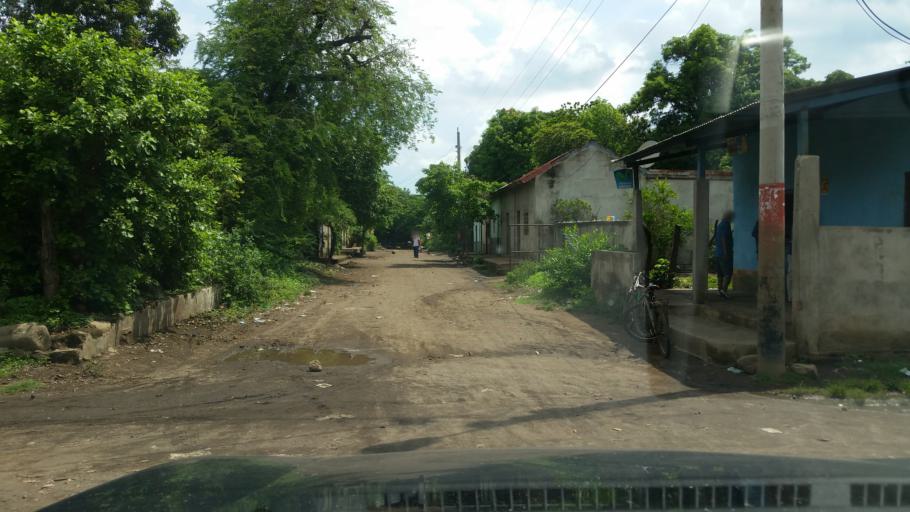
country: NI
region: Chinandega
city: Puerto Morazan
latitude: 12.7664
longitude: -87.1337
